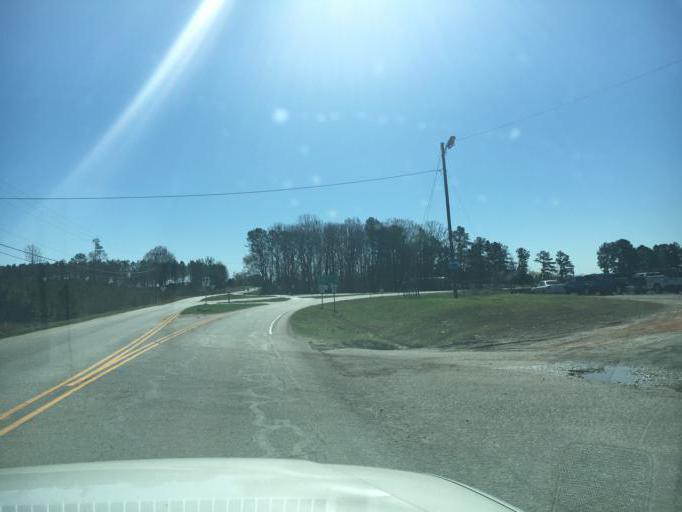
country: US
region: South Carolina
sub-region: Greenwood County
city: Ninety Six
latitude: 34.2208
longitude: -82.0382
